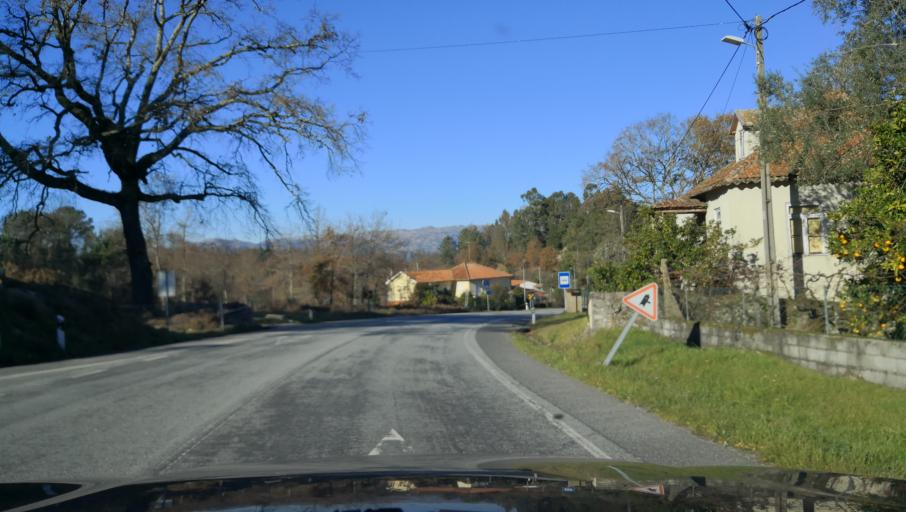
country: PT
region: Viseu
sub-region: Vouzela
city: Vouzela
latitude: 40.7069
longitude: -8.1441
